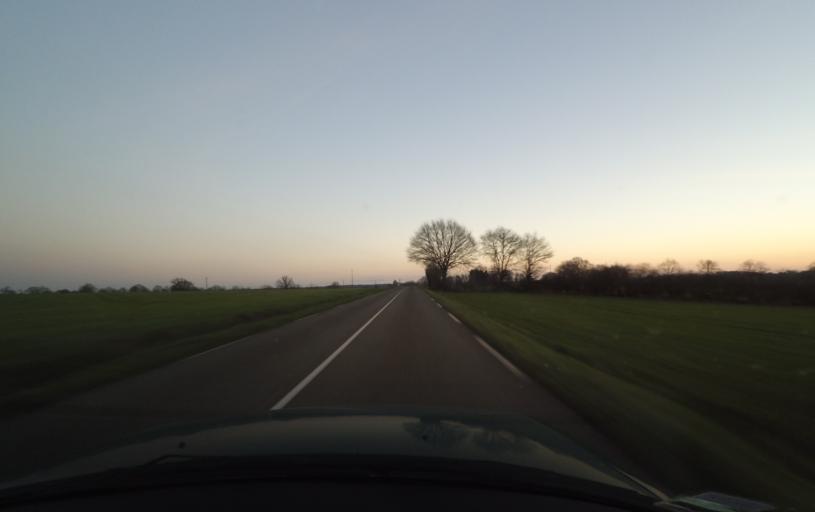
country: FR
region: Pays de la Loire
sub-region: Departement de la Mayenne
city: Soulge-sur-Ouette
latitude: 48.0907
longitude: -0.5300
